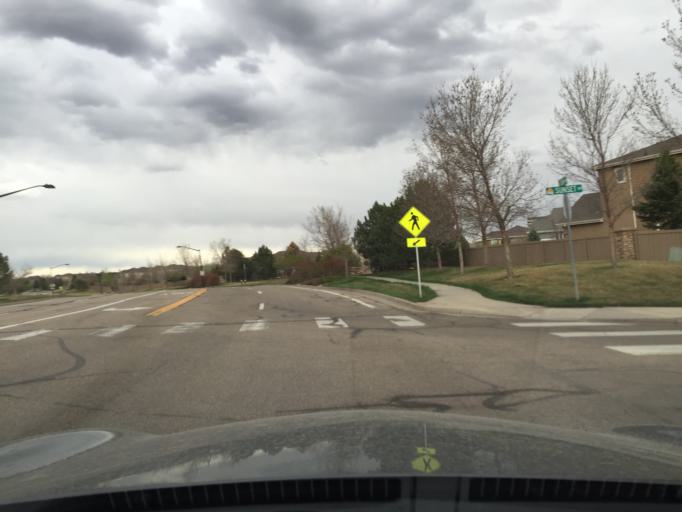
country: US
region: Colorado
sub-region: Boulder County
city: Erie
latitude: 40.0057
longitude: -105.0304
